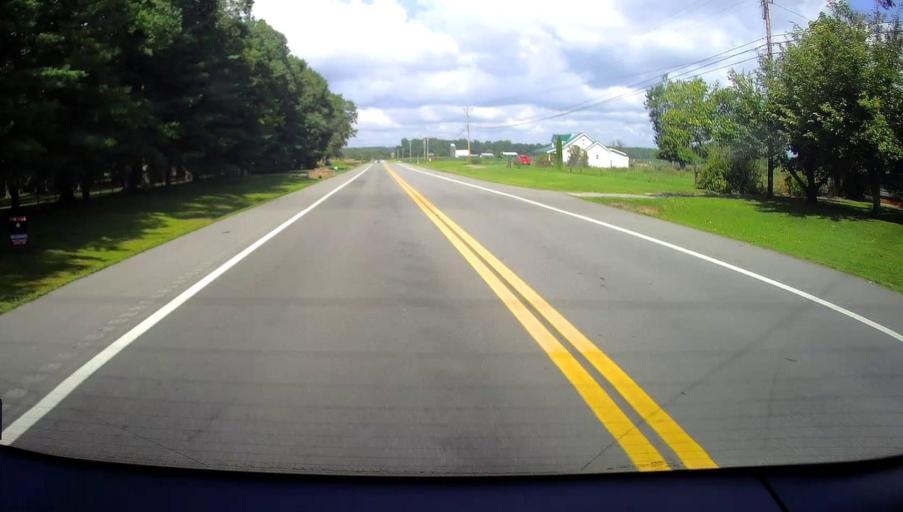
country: US
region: Tennessee
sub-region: Coffee County
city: New Union
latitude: 35.5204
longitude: -86.1456
